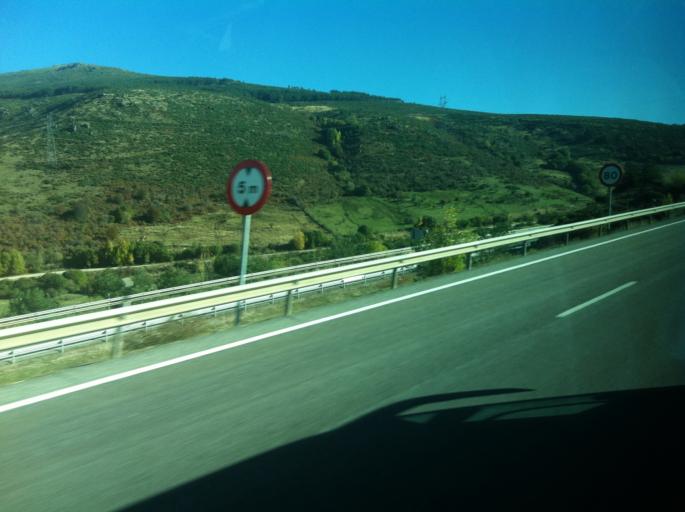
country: ES
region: Madrid
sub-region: Provincia de Madrid
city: Somosierra
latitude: 41.1435
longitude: -3.5823
